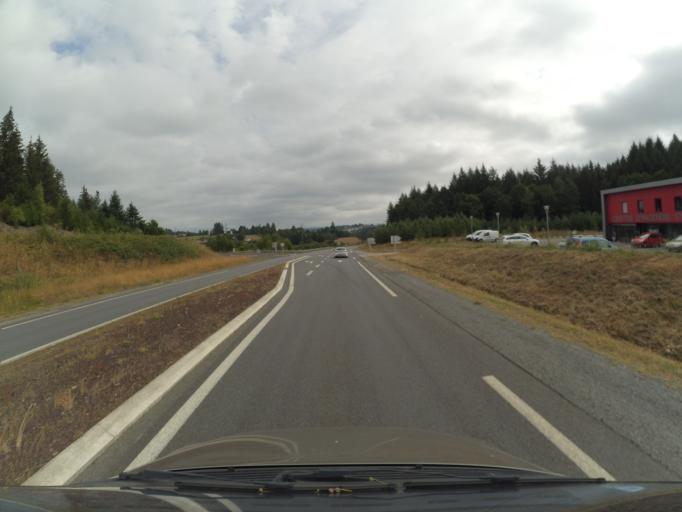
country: FR
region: Limousin
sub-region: Departement de la Correze
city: Ussel
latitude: 45.5275
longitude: 2.2946
